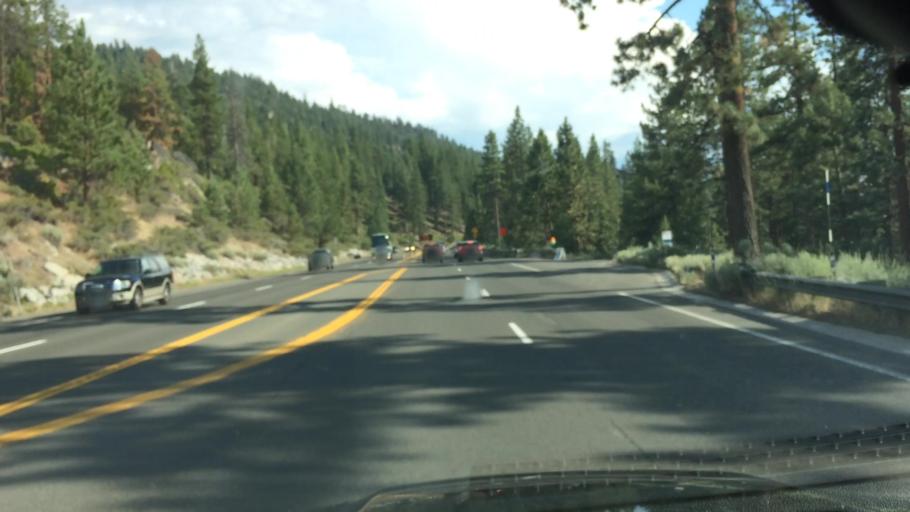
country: US
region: Nevada
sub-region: Douglas County
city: Kingsbury
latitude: 39.0735
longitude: -119.9408
